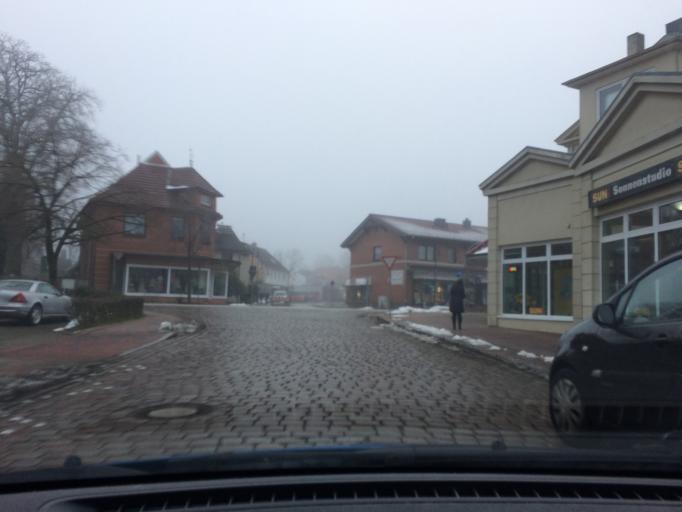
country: DE
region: Schleswig-Holstein
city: Schwarzenbek
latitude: 53.5020
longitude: 10.4831
